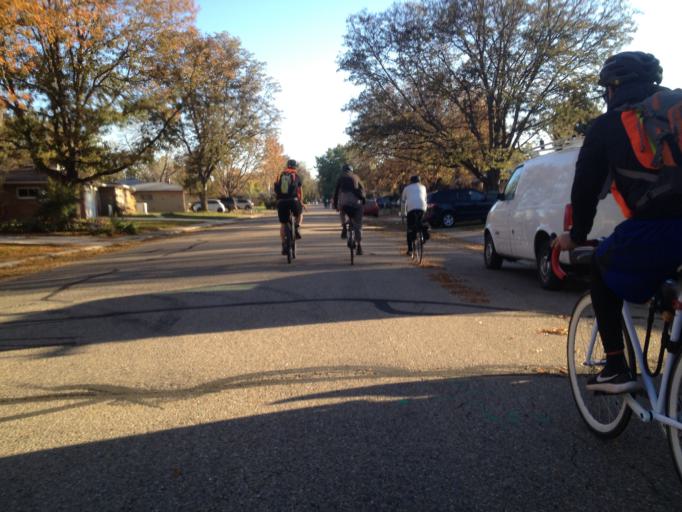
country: US
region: Colorado
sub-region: Boulder County
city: Longmont
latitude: 40.1806
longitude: -105.1144
